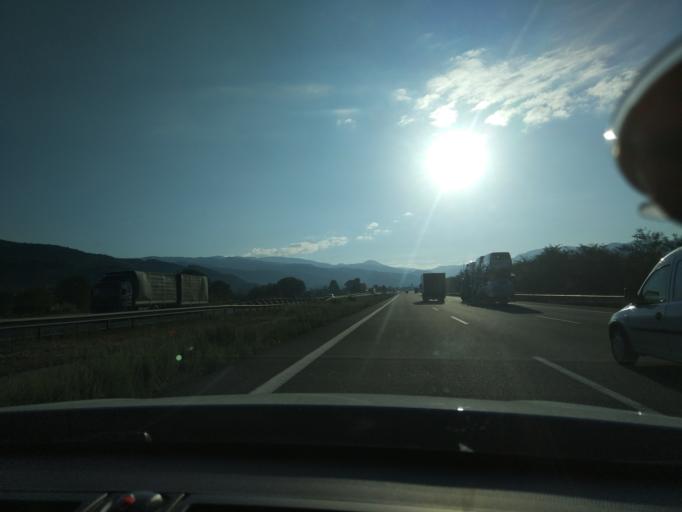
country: TR
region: Duzce
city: Kaynasli
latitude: 40.7829
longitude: 31.3101
